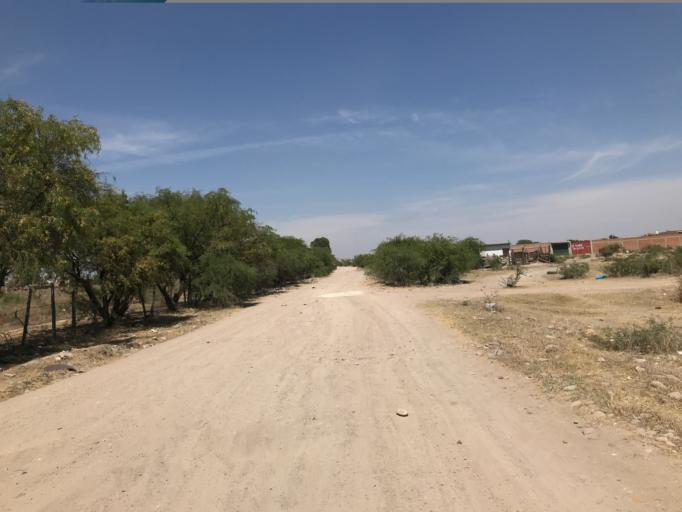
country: MX
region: Durango
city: Victoria de Durango
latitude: 23.9817
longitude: -104.6873
